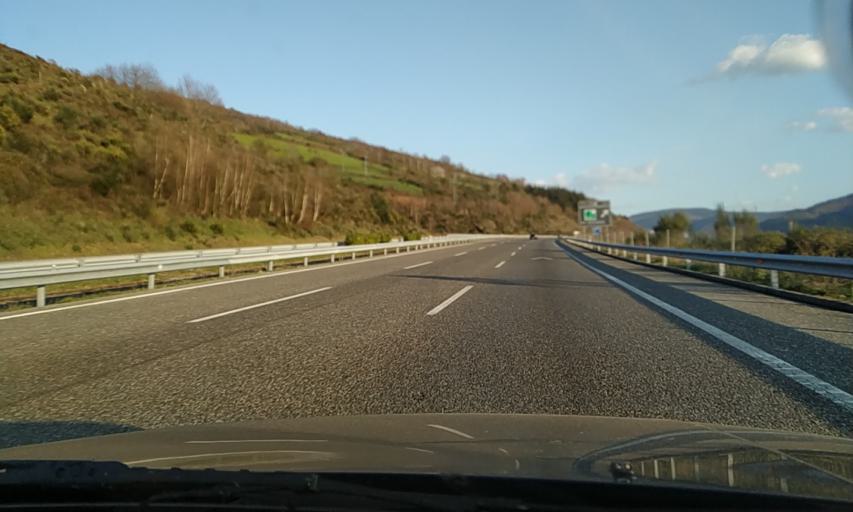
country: ES
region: Galicia
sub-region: Provincia de Lugo
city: San Roman
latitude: 42.7728
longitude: -7.0933
